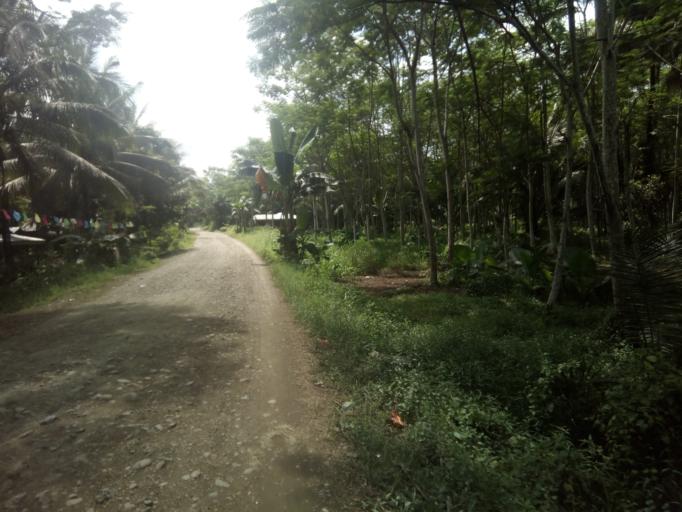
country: PH
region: Caraga
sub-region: Province of Agusan del Sur
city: Santa Josefa
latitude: 8.0292
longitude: 126.0158
